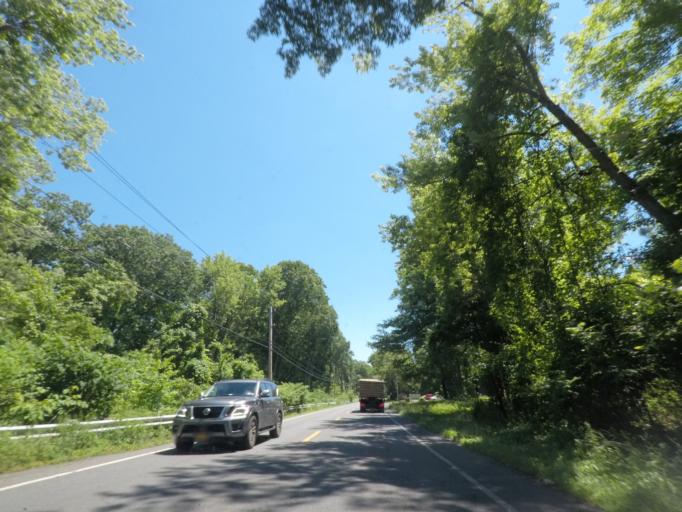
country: US
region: Massachusetts
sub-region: Hampden County
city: Westfield
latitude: 42.1451
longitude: -72.8106
